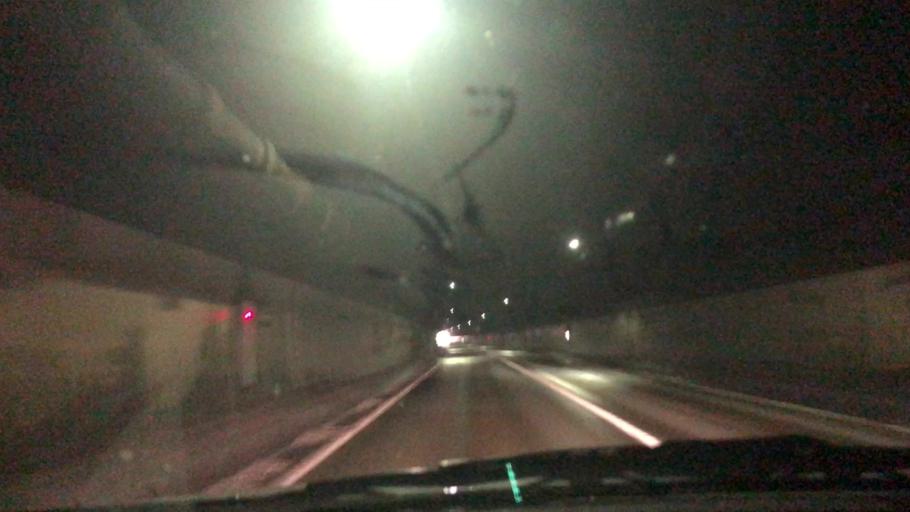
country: JP
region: Hokkaido
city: Shimo-furano
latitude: 42.9056
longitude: 142.3340
